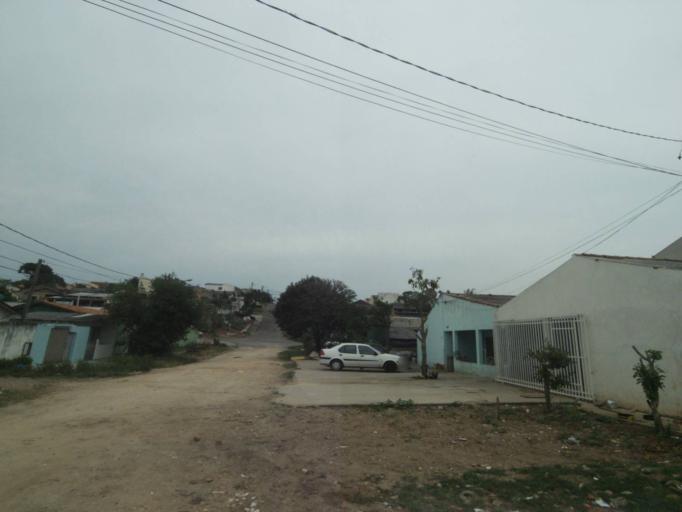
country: BR
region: Parana
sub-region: Pinhais
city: Pinhais
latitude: -25.4097
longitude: -49.1972
